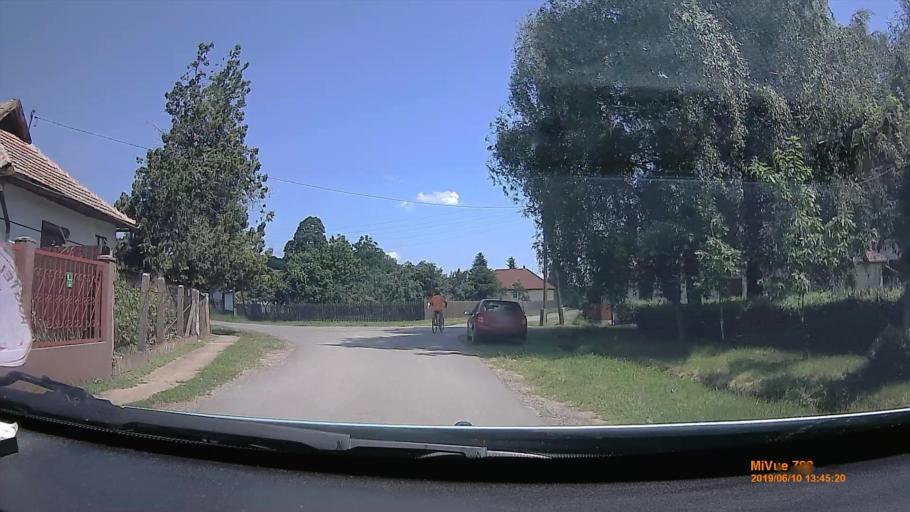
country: HU
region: Szabolcs-Szatmar-Bereg
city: Tiszadob
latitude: 48.0094
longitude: 21.1682
